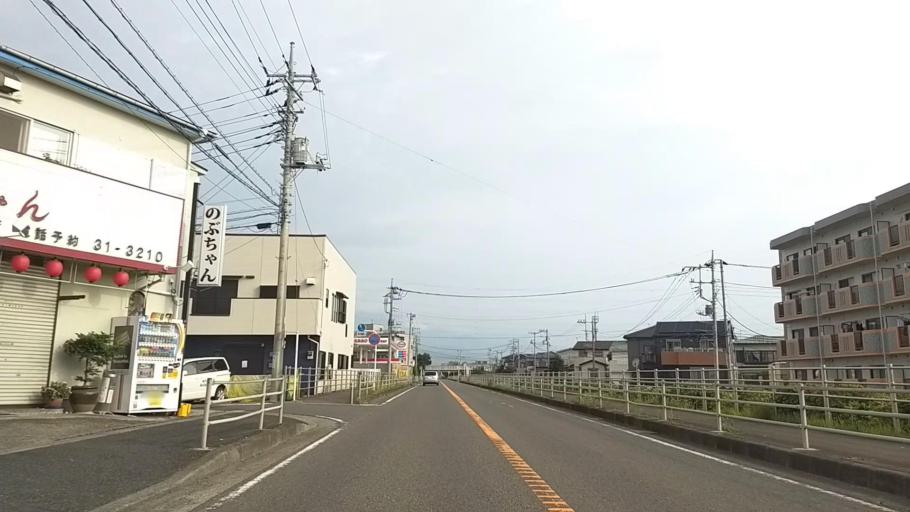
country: JP
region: Kanagawa
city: Hiratsuka
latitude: 35.3390
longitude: 139.3094
